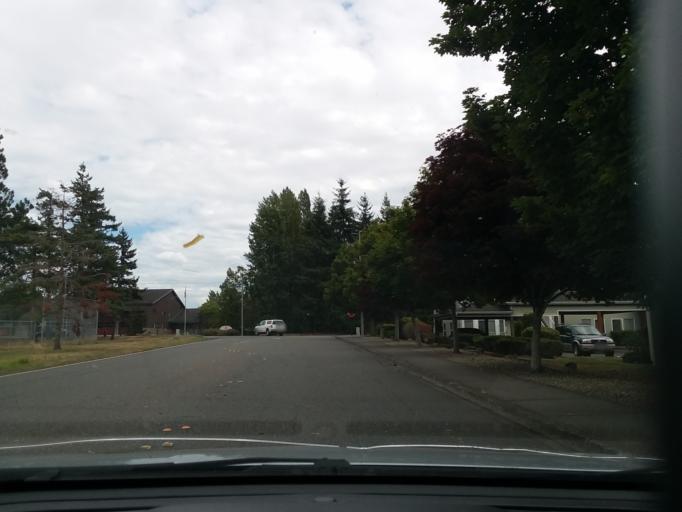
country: US
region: Washington
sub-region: Whatcom County
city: Bellingham
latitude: 48.7878
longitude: -122.4795
